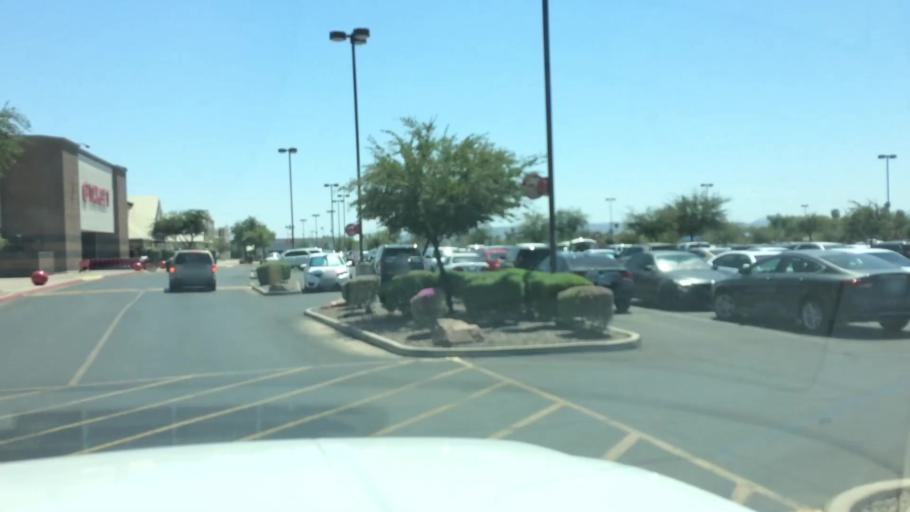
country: US
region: Arizona
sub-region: Maricopa County
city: Paradise Valley
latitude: 33.4781
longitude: -111.9847
